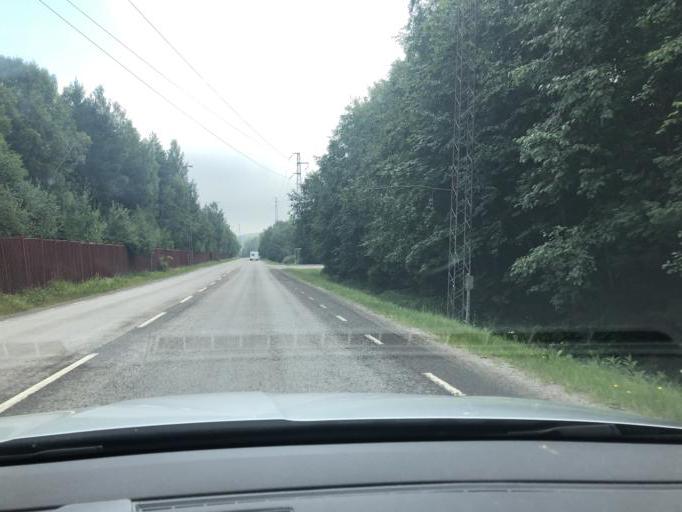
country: SE
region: Vaesternorrland
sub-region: Sundsvalls Kommun
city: Sundsvall
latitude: 62.4112
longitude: 17.3229
